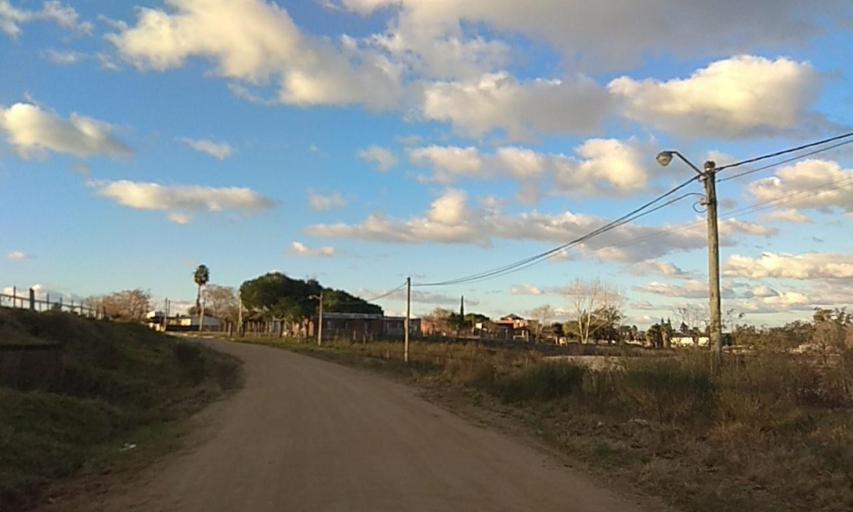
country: UY
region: Florida
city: Florida
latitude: -34.1065
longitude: -56.2315
